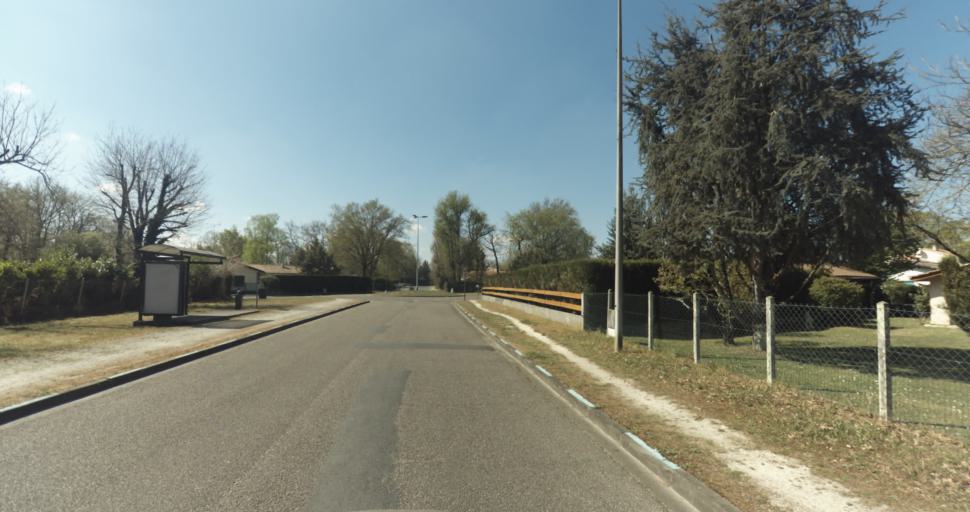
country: FR
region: Aquitaine
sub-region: Departement de la Gironde
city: Martignas-sur-Jalle
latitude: 44.8026
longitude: -0.7874
